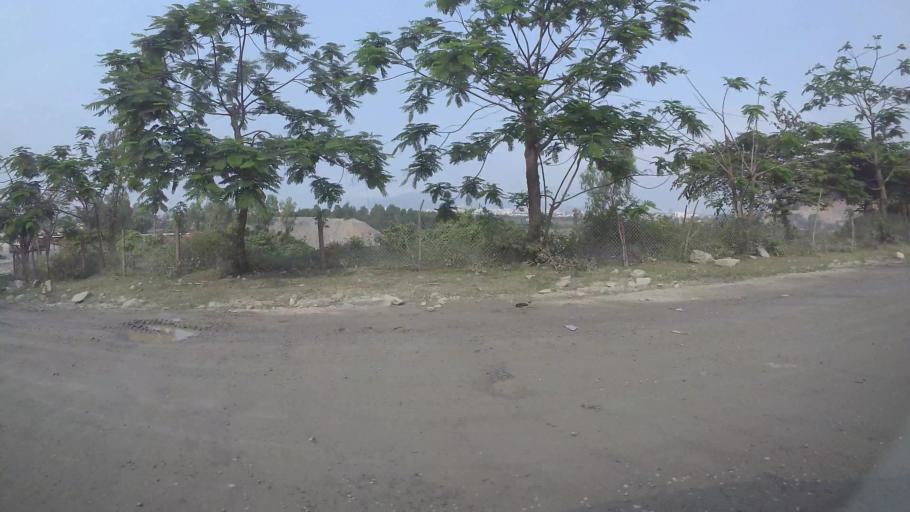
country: VN
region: Da Nang
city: Lien Chieu
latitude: 16.0414
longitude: 108.1499
